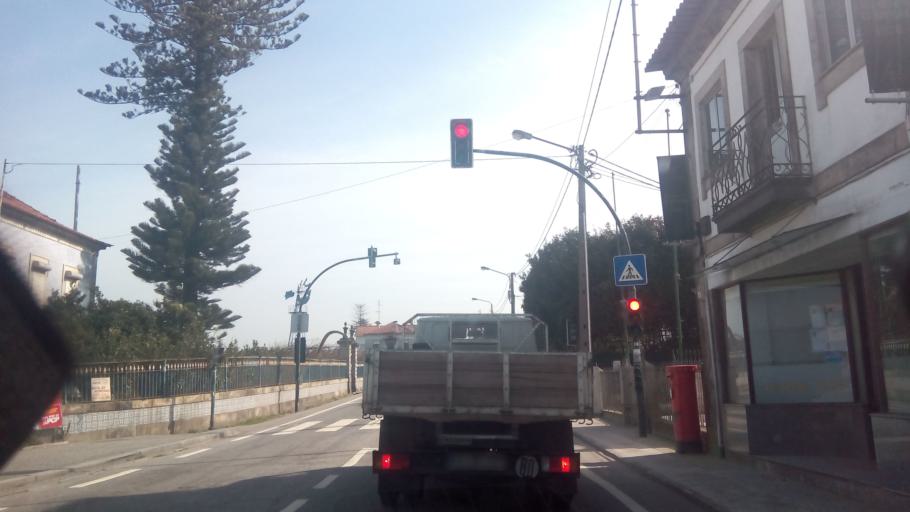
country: PT
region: Viana do Castelo
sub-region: Viana do Castelo
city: Darque
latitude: 41.6826
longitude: -8.7889
